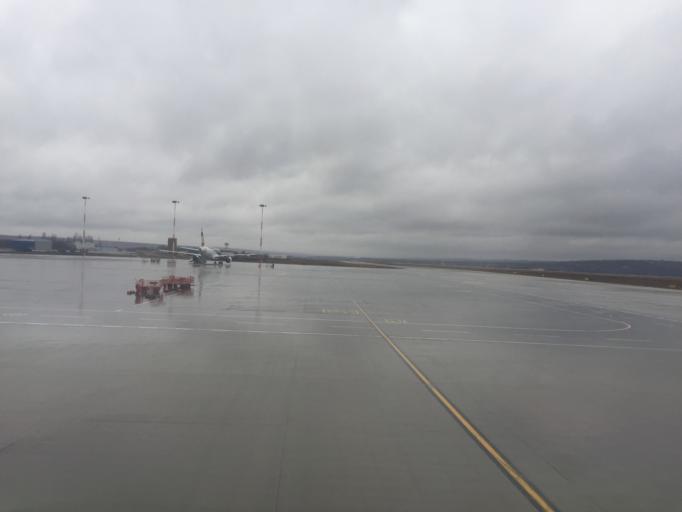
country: MD
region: Chisinau
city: Singera
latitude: 46.9321
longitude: 28.9345
